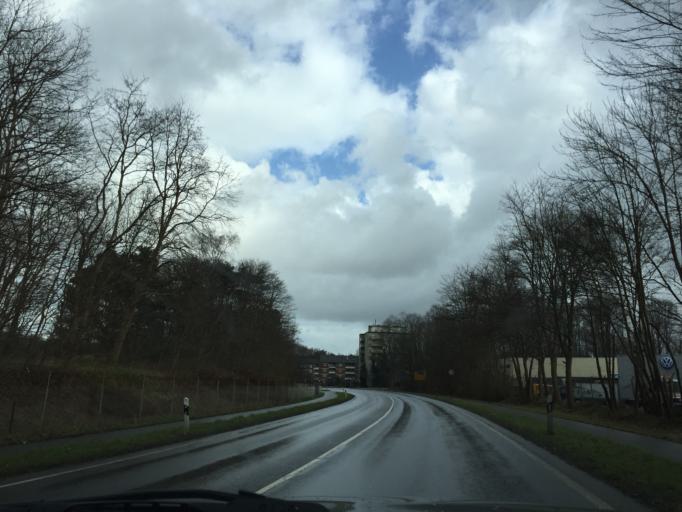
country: DE
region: North Rhine-Westphalia
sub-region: Regierungsbezirk Dusseldorf
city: Emmerich
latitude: 51.8474
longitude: 6.2387
